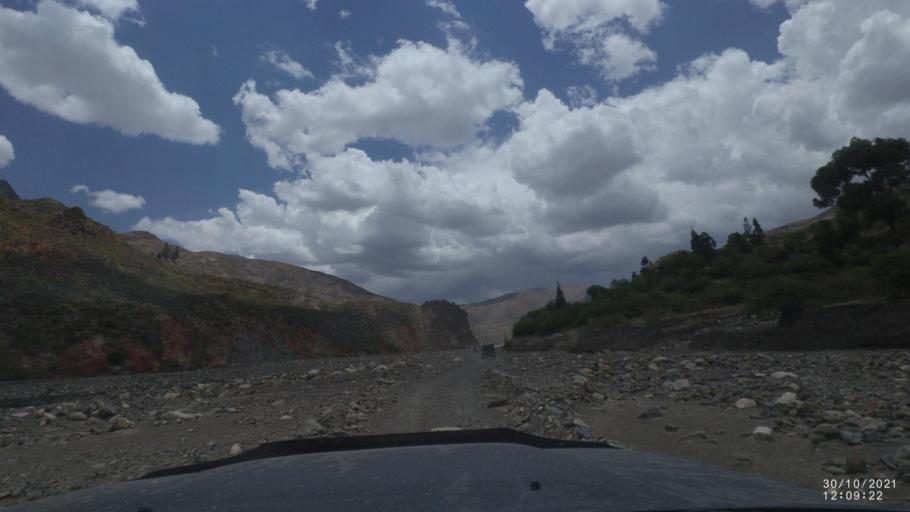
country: BO
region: Cochabamba
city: Colchani
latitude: -17.5459
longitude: -66.6272
